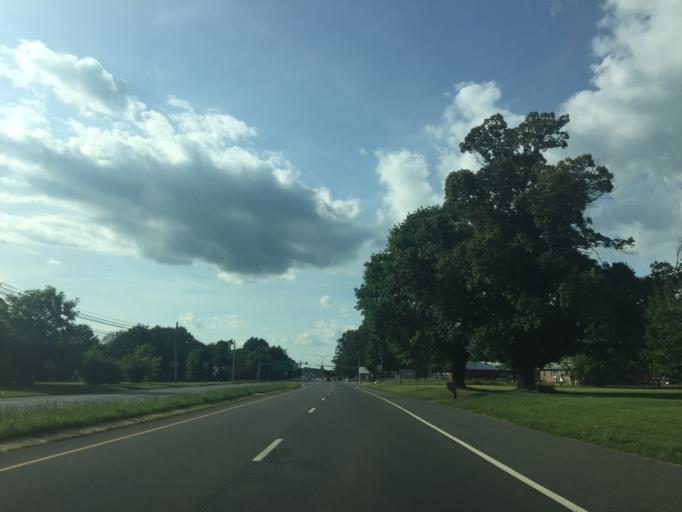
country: US
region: Delaware
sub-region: Kent County
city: Smyrna
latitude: 39.2895
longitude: -75.5957
